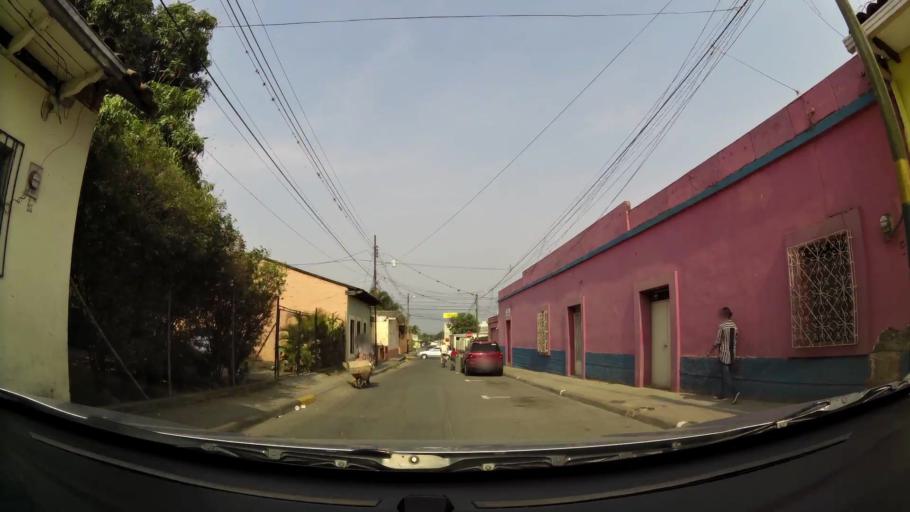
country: HN
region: Comayagua
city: Comayagua
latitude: 14.4586
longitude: -87.6430
